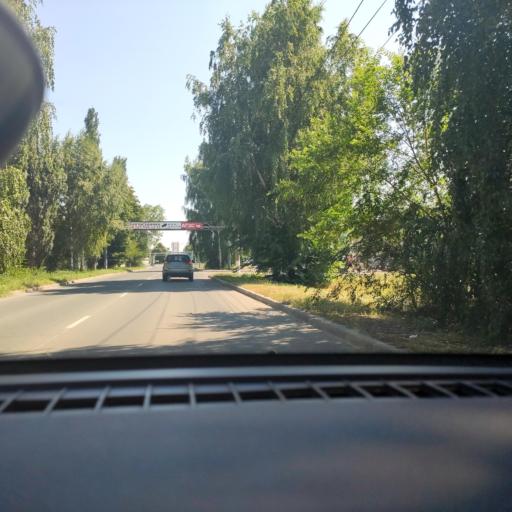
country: RU
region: Samara
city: Bereza
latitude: 53.5133
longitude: 50.1428
